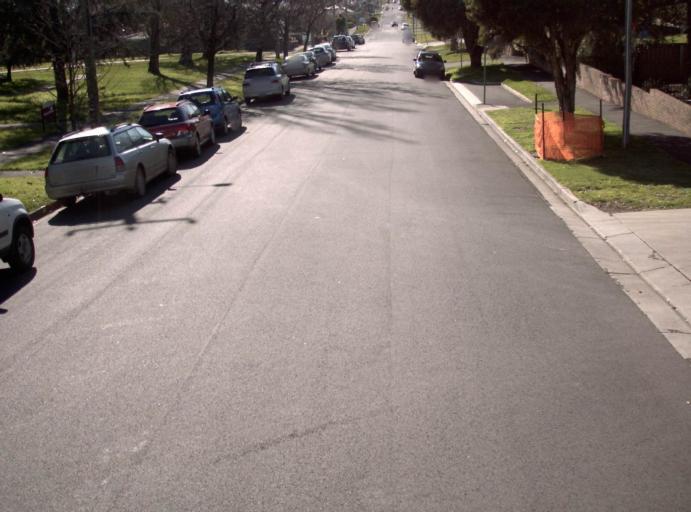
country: AU
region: Tasmania
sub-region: Launceston
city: East Launceston
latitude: -41.4516
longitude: 147.1584
